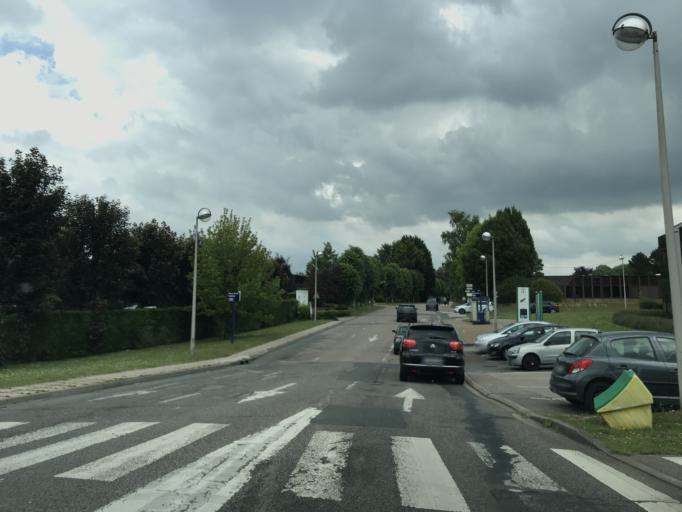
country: FR
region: Haute-Normandie
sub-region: Departement de la Seine-Maritime
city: Mont-Saint-Aignan
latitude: 49.4767
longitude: 1.0933
